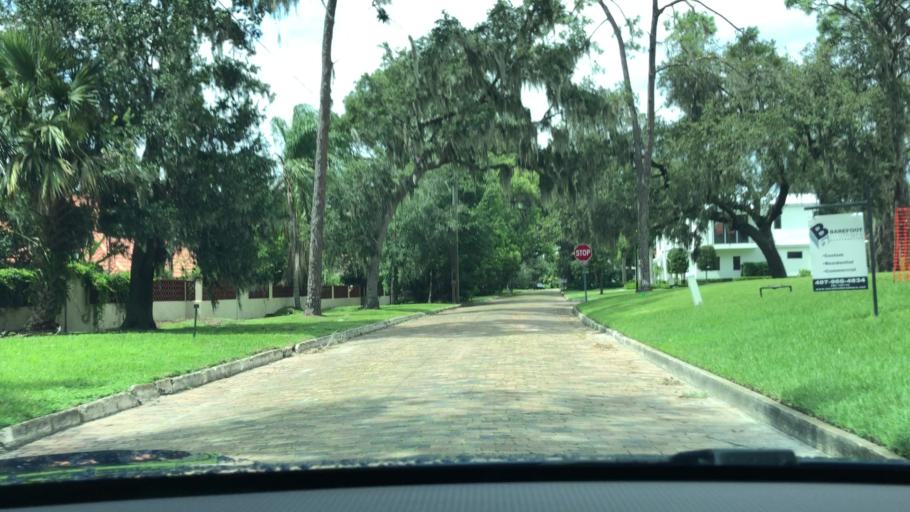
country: US
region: Florida
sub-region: Orange County
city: Winter Park
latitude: 28.5806
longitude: -81.3524
